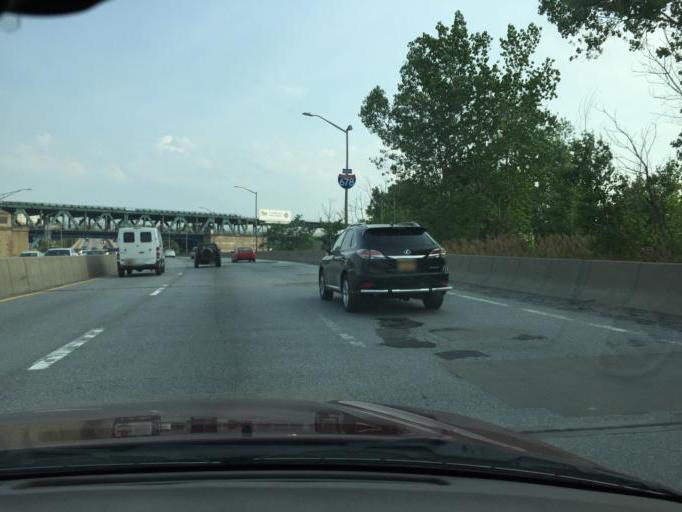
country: US
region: New York
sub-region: Queens County
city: Jamaica
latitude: 40.7588
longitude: -73.8389
